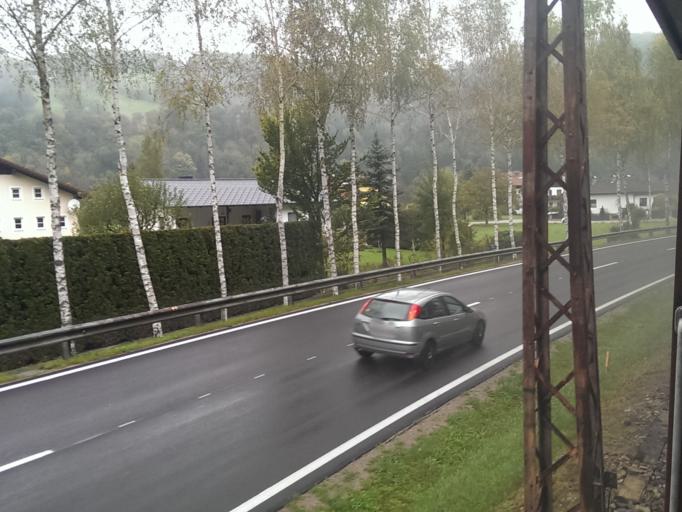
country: AT
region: Lower Austria
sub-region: Politischer Bezirk Sankt Polten
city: Rabenstein an der Pielach
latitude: 48.0523
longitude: 15.4537
